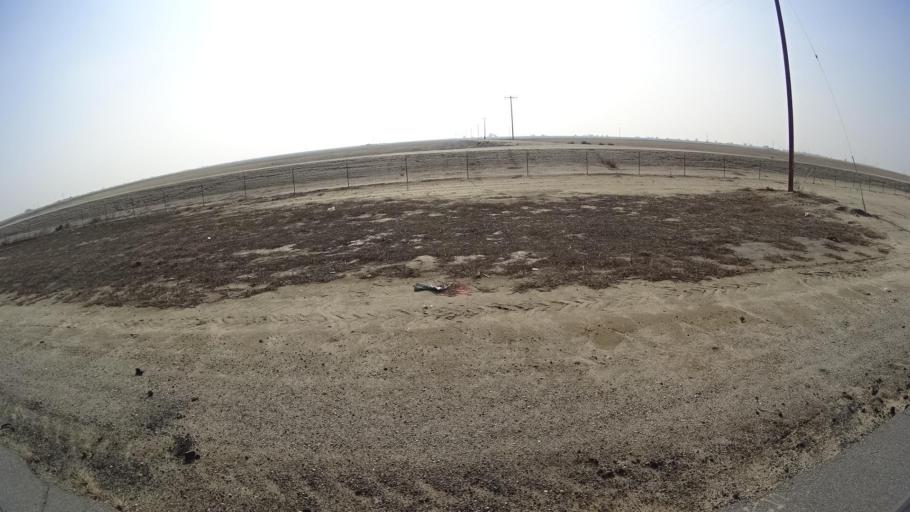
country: US
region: California
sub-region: Kern County
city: Rosedale
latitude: 35.3544
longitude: -119.2612
